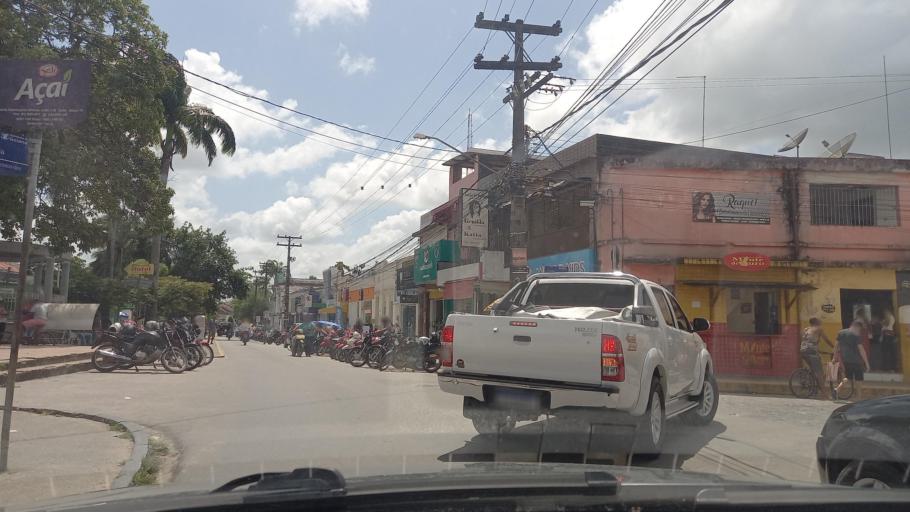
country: BR
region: Pernambuco
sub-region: Goiana
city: Goiana
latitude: -7.5610
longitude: -34.9989
